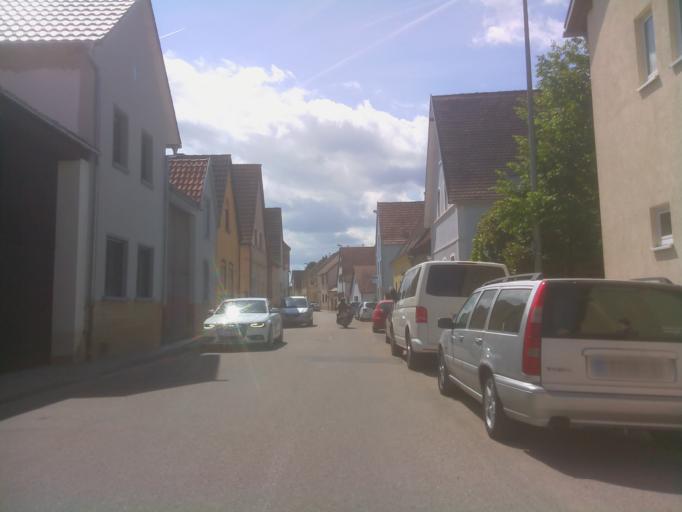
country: DE
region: Rheinland-Pfalz
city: Neuhofen
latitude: 49.4208
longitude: 8.4298
